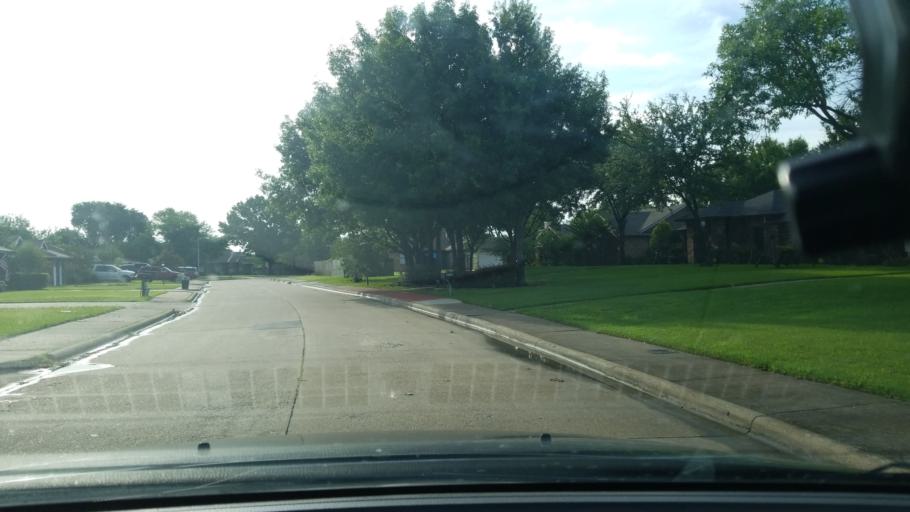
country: US
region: Texas
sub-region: Dallas County
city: Mesquite
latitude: 32.8009
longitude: -96.6076
